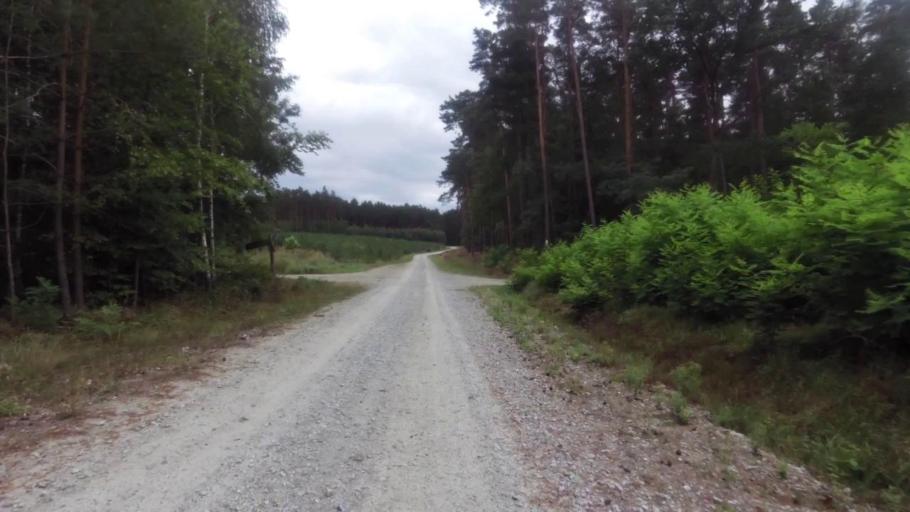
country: PL
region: Lubusz
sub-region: Powiat gorzowski
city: Kostrzyn nad Odra
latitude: 52.6537
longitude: 14.6373
